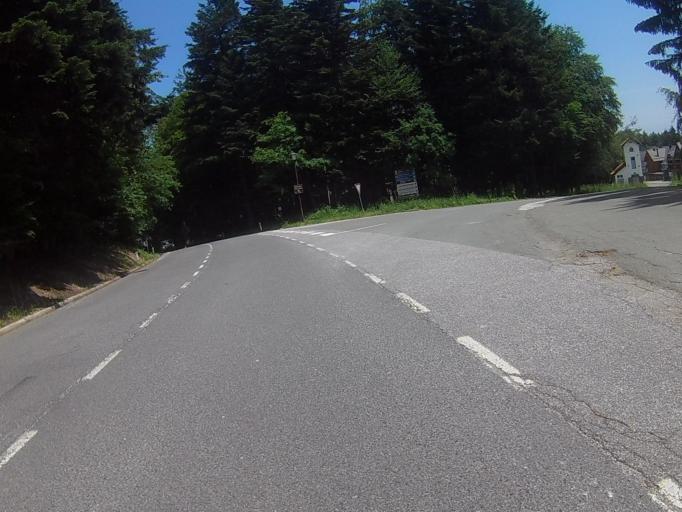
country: SI
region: Maribor
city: Pekre
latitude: 46.5145
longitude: 15.5761
